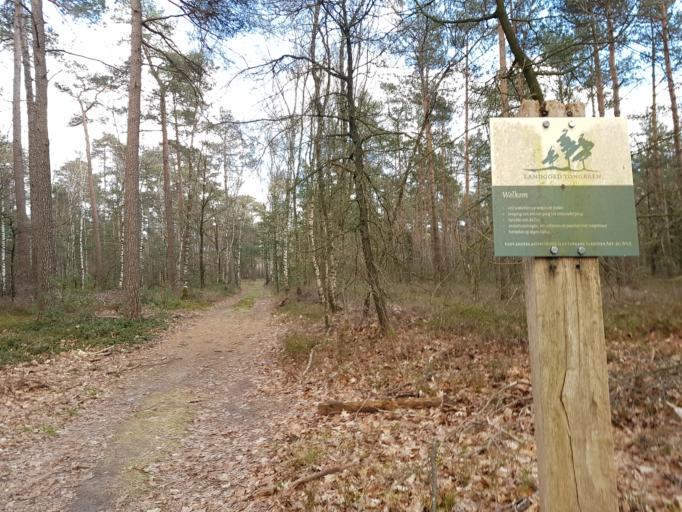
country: NL
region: Gelderland
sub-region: Gemeente Epe
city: Emst
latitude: 52.3429
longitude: 5.9125
